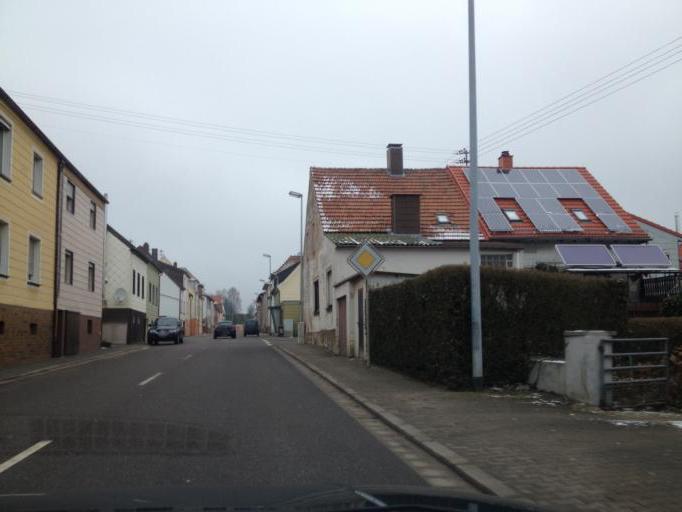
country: DE
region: Saarland
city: Bexbach
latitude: 49.3831
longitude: 7.2574
